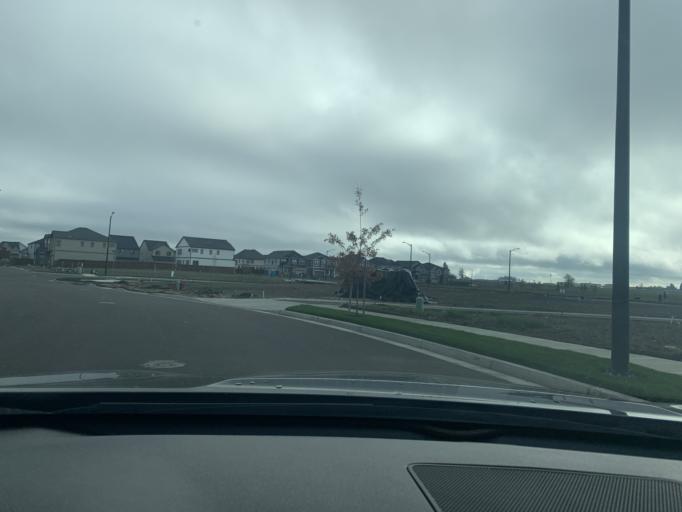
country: US
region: Oregon
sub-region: Washington County
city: North Plains
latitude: 45.5943
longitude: -122.9773
